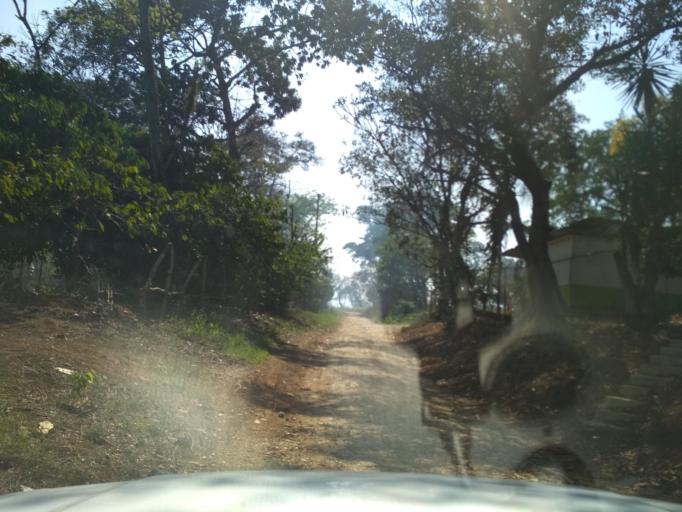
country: MX
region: Veracruz
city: Amatlan de los Reyes
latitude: 18.8483
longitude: -96.9050
